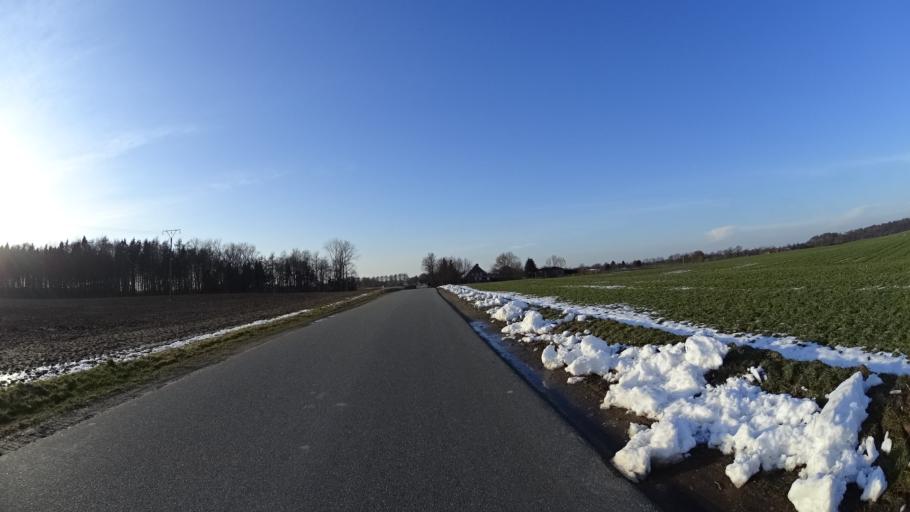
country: DE
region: Schleswig-Holstein
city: Fargau-Pratjau
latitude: 54.3372
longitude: 10.4104
